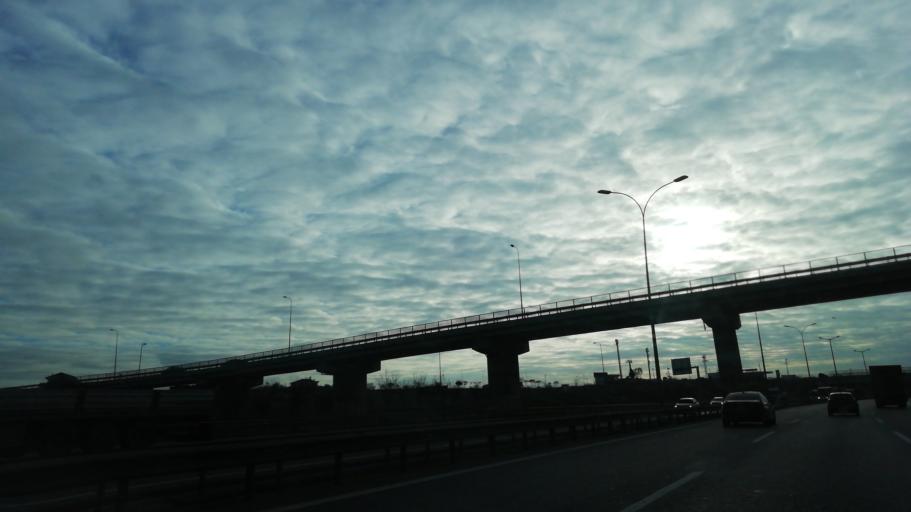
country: TR
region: Istanbul
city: Sultanbeyli
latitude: 40.9290
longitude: 29.3471
